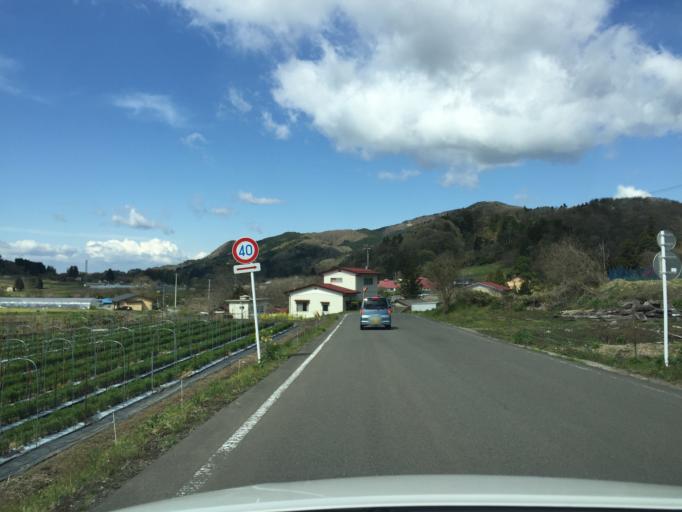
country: JP
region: Fukushima
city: Funehikimachi-funehiki
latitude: 37.5596
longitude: 140.6615
